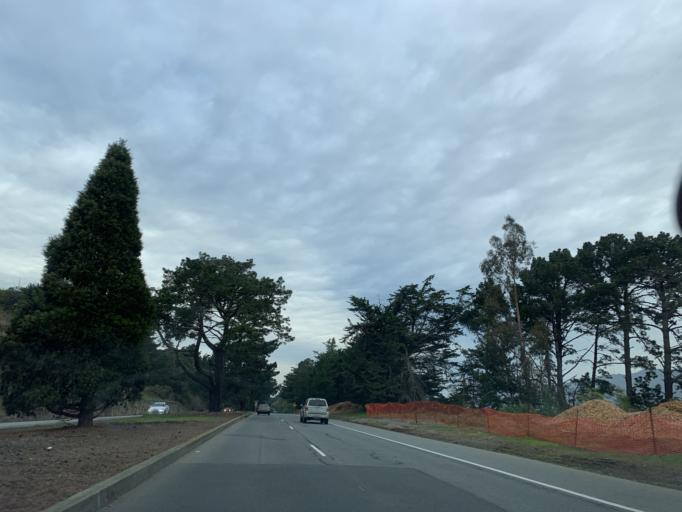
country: US
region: California
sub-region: San Mateo County
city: Colma
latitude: 37.6510
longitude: -122.4514
